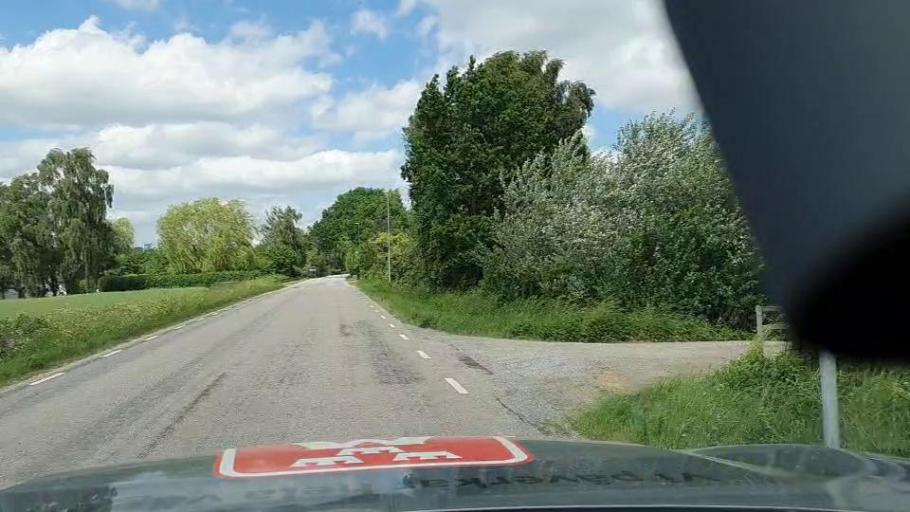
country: SE
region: Blekinge
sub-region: Karlshamns Kommun
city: Morrum
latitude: 56.1043
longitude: 14.6850
